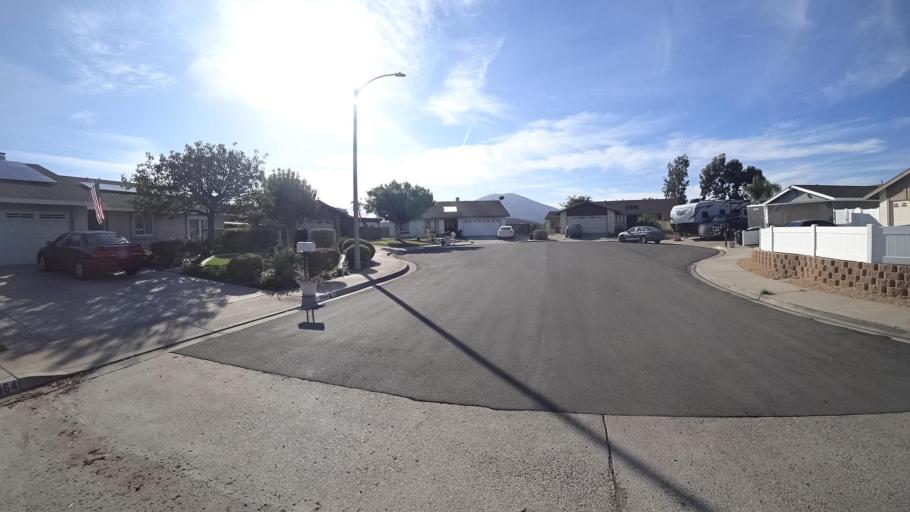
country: US
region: California
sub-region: San Diego County
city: Rancho San Diego
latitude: 32.7402
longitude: -116.9576
